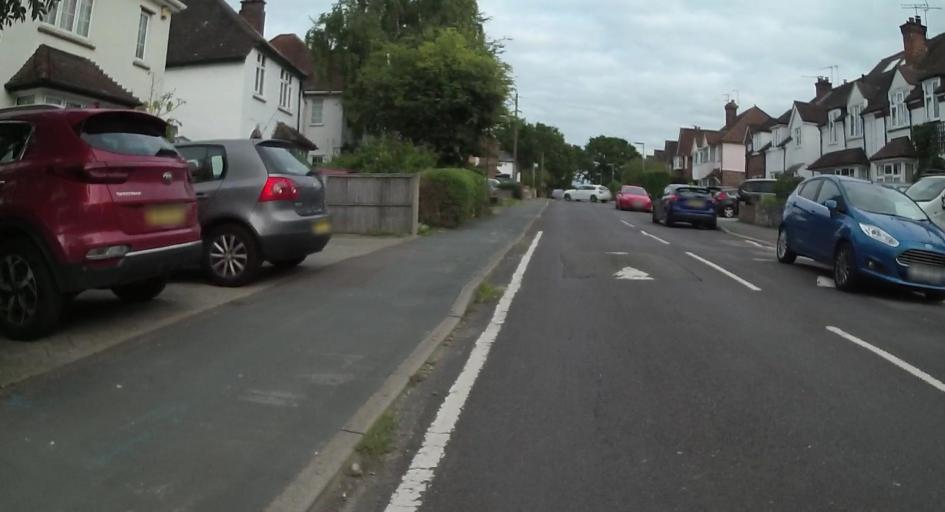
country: GB
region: England
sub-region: Surrey
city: Knaphill
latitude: 51.3175
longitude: -0.6114
